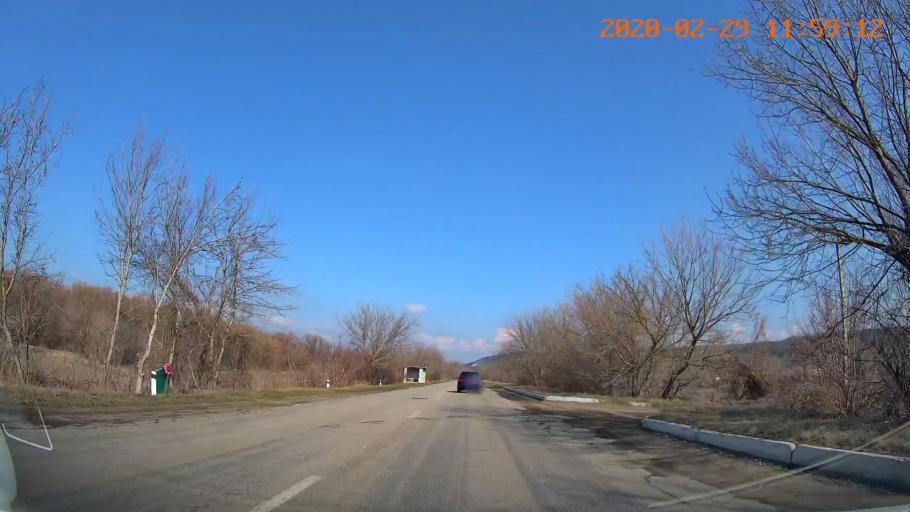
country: MD
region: Telenesti
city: Ribnita
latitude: 47.8224
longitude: 29.0156
